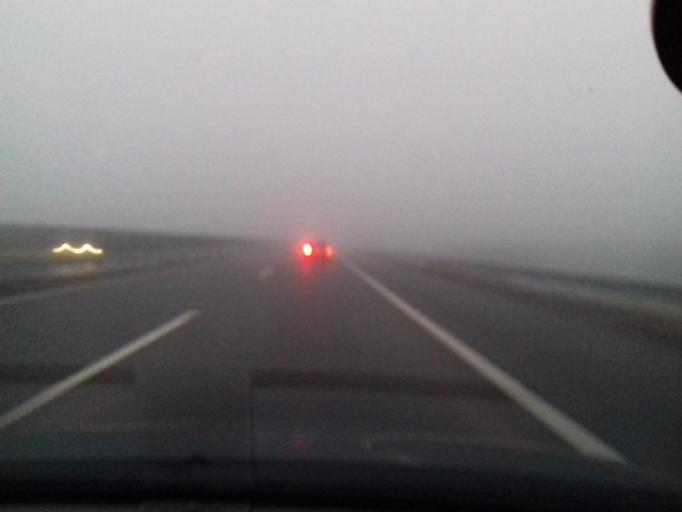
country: HU
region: Hajdu-Bihar
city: Hajdunanas
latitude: 47.8818
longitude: 21.4107
